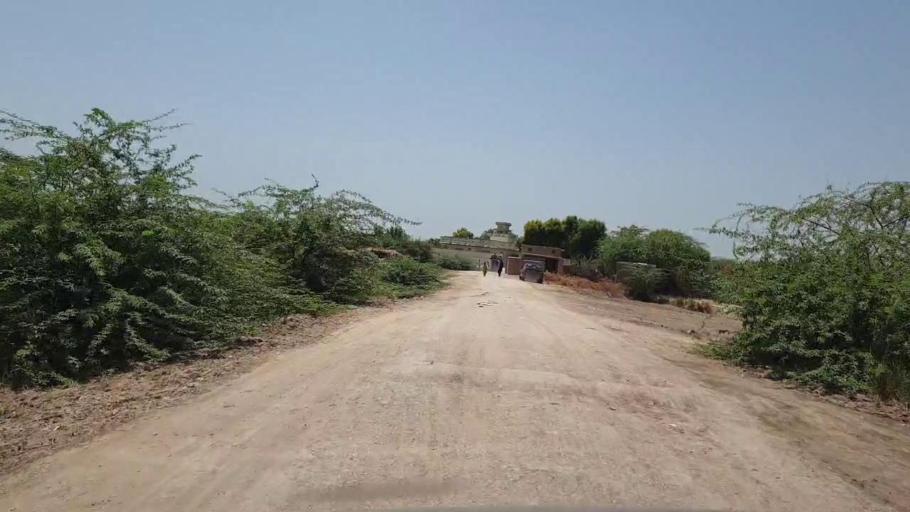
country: PK
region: Sindh
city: Sakrand
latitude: 26.1091
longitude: 68.3899
